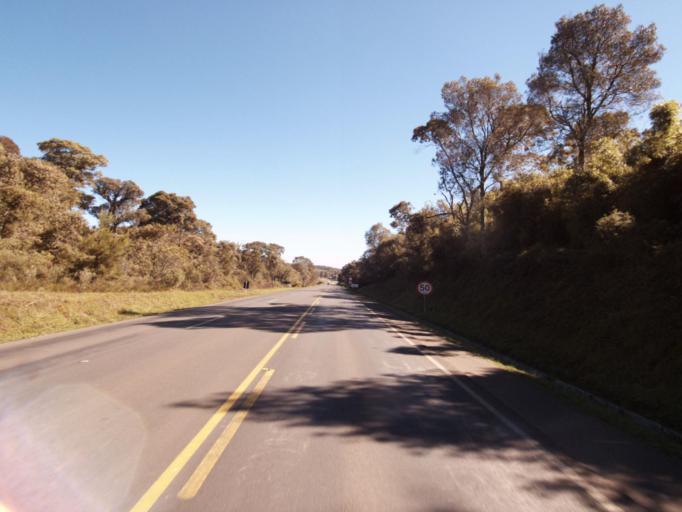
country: BR
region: Santa Catarina
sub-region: Concordia
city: Concordia
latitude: -26.9722
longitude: -51.8464
